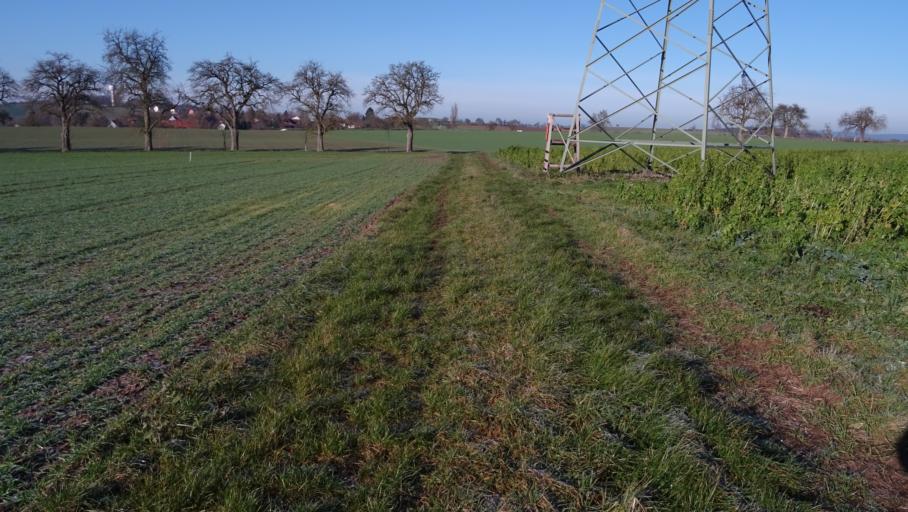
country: DE
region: Baden-Wuerttemberg
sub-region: Karlsruhe Region
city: Mosbach
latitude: 49.3431
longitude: 9.1868
